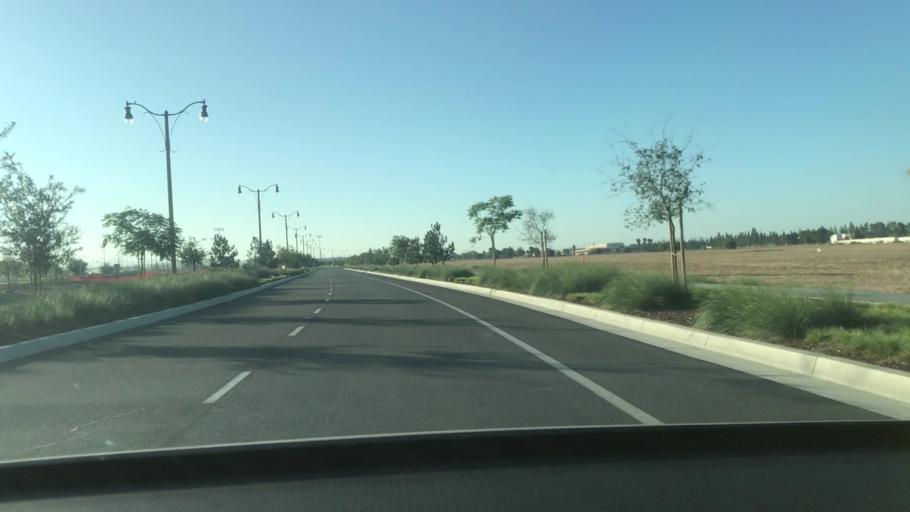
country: US
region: California
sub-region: Orange County
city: Lake Forest
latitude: 33.6727
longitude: -117.7505
